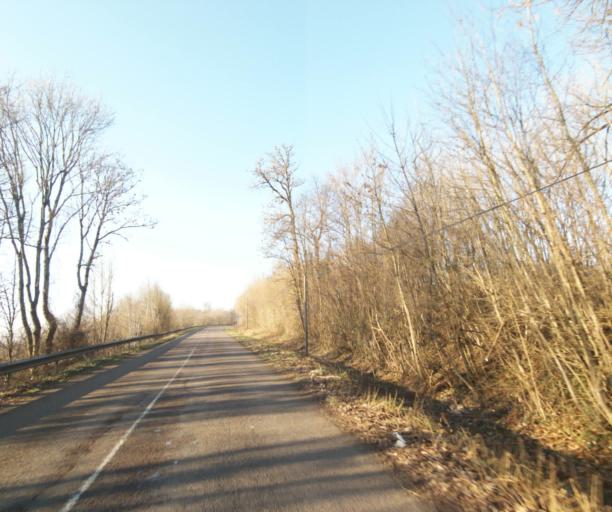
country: FR
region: Champagne-Ardenne
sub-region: Departement de la Haute-Marne
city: Chevillon
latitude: 48.5469
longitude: 5.0989
